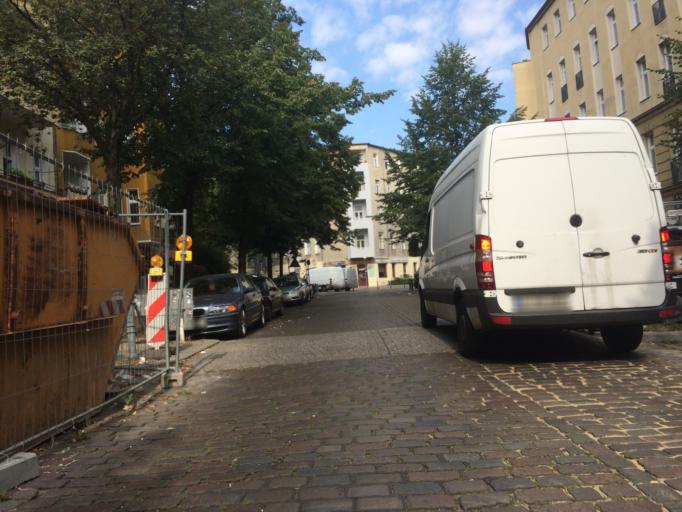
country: DE
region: Berlin
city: Wedding Bezirk
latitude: 52.5505
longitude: 13.3629
